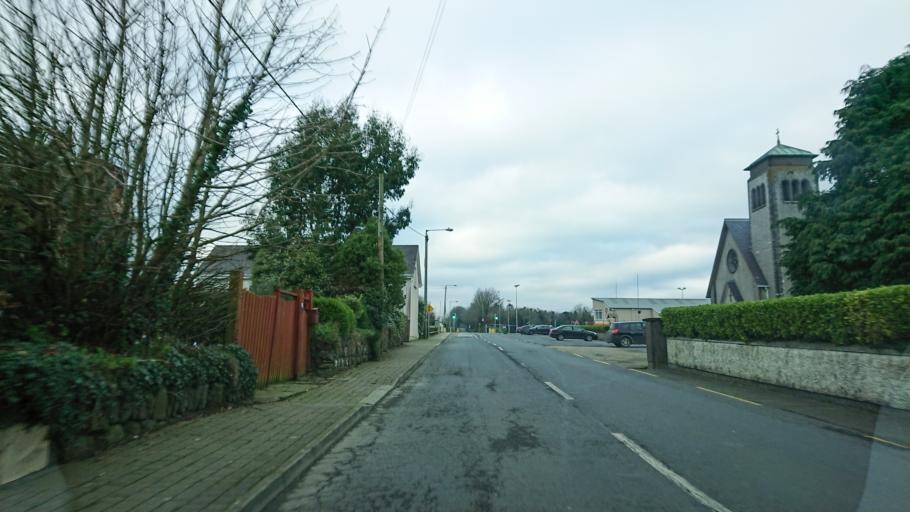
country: IE
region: Munster
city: Carrick-on-Suir
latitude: 52.3060
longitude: -7.4982
